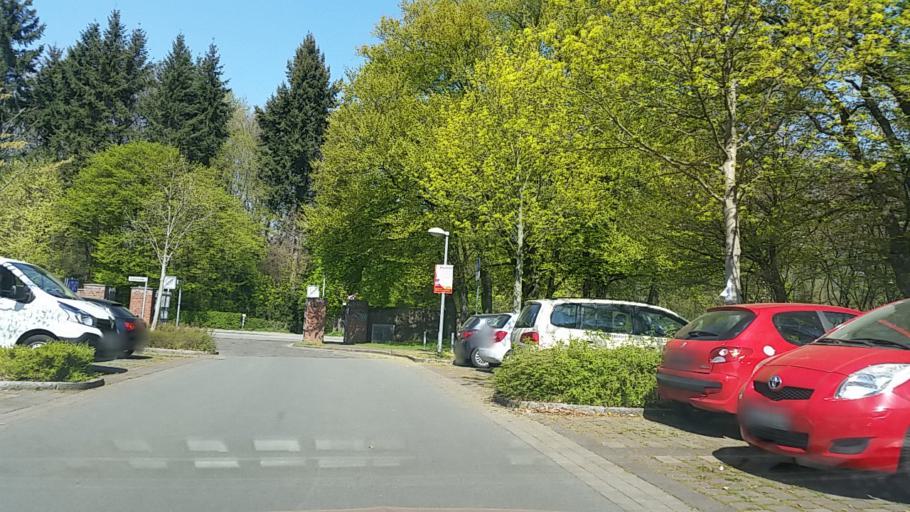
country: DE
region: Schleswig-Holstein
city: Wentorf bei Hamburg
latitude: 53.4887
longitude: 10.2464
